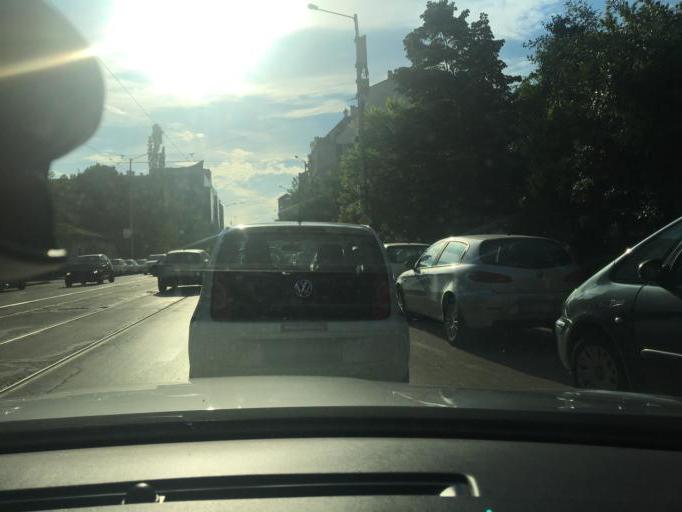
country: BG
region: Sofia-Capital
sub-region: Stolichna Obshtina
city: Sofia
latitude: 42.6790
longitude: 23.3636
